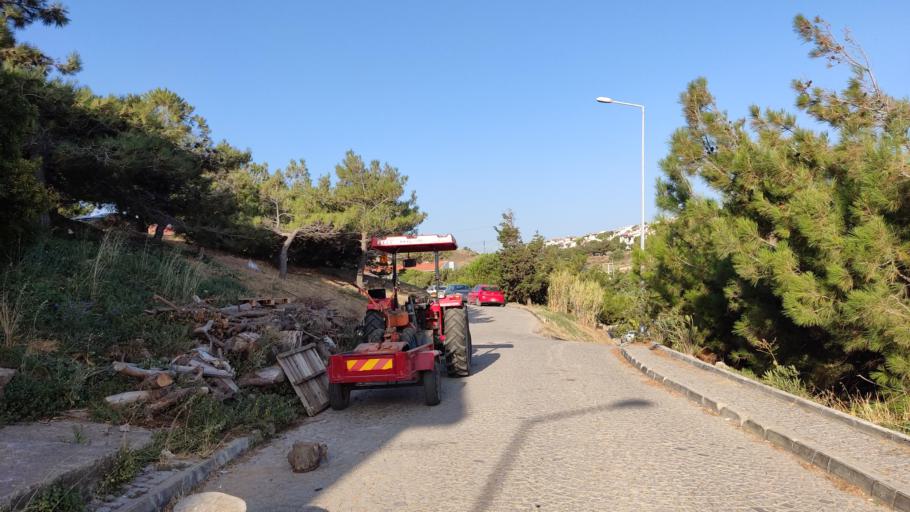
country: TR
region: Canakkale
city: Bozcaada
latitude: 39.8325
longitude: 26.0684
